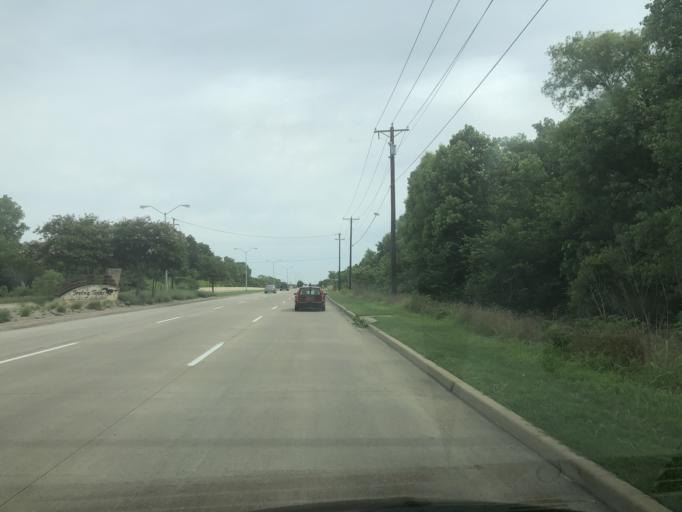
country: US
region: Texas
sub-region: Dallas County
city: Grand Prairie
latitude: 32.7864
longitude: -96.9946
